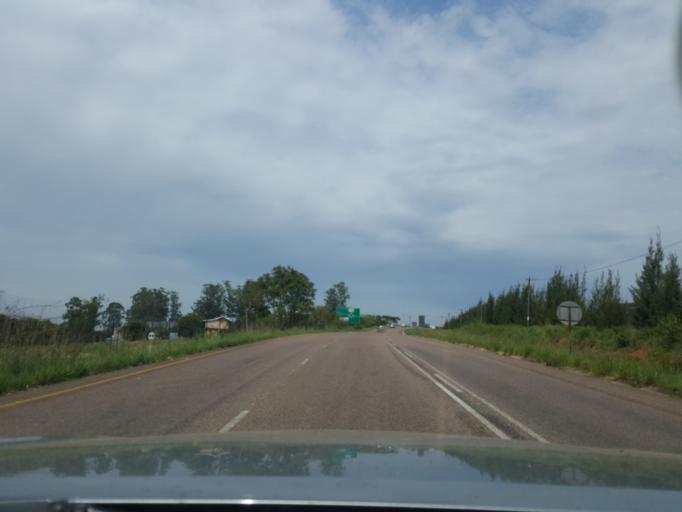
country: ZA
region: Mpumalanga
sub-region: Ehlanzeni District
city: White River
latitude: -25.3056
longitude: 31.0358
